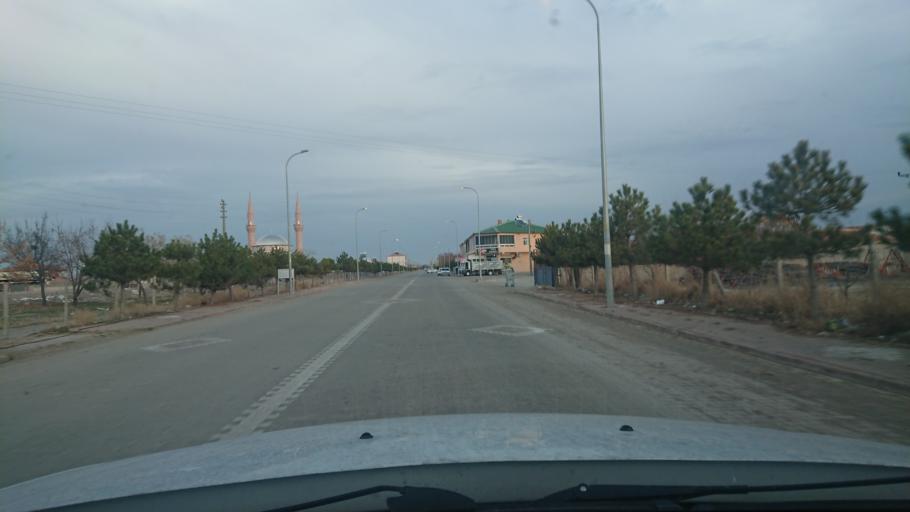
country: TR
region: Aksaray
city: Yesilova
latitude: 38.3317
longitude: 33.7521
